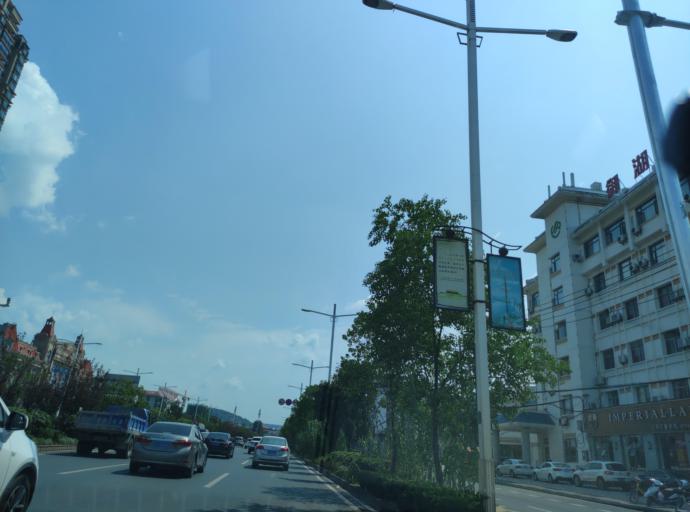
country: CN
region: Jiangxi Sheng
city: Pingxiang
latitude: 27.6563
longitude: 113.8911
